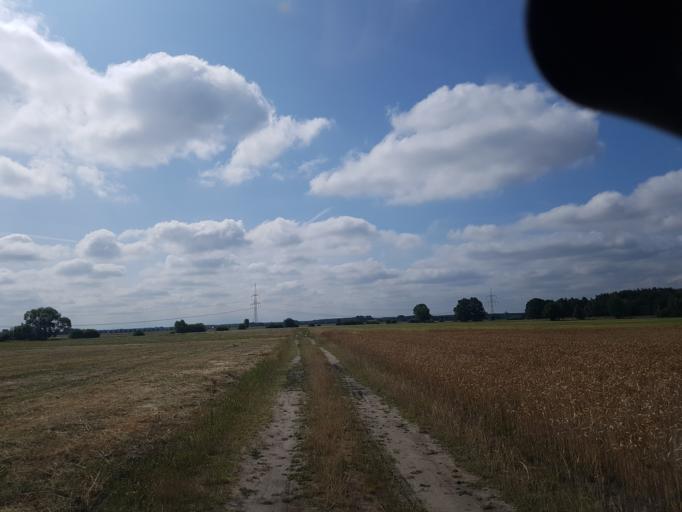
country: DE
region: Brandenburg
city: Schonborn
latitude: 51.5852
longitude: 13.5138
